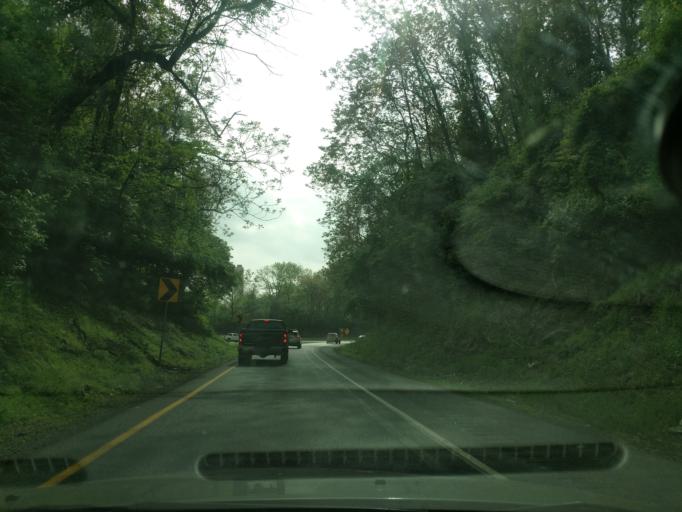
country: US
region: Pennsylvania
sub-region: Berks County
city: Mount Penn
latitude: 40.3086
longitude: -75.9016
